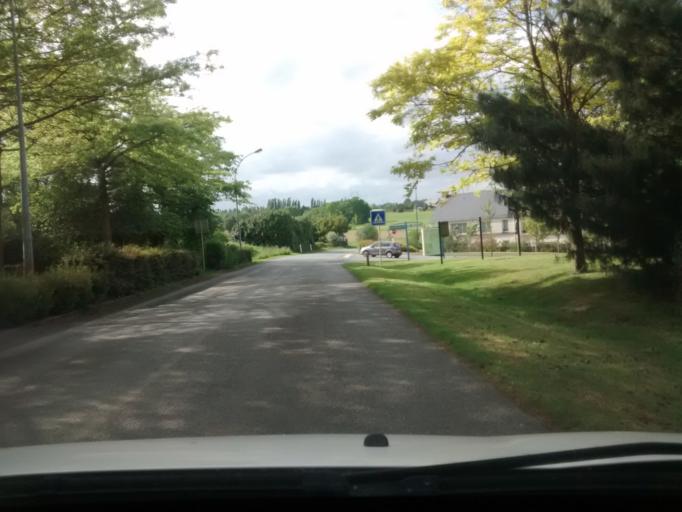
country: FR
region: Brittany
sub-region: Departement d'Ille-et-Vilaine
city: Chateaugiron
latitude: 48.0646
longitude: -1.5275
